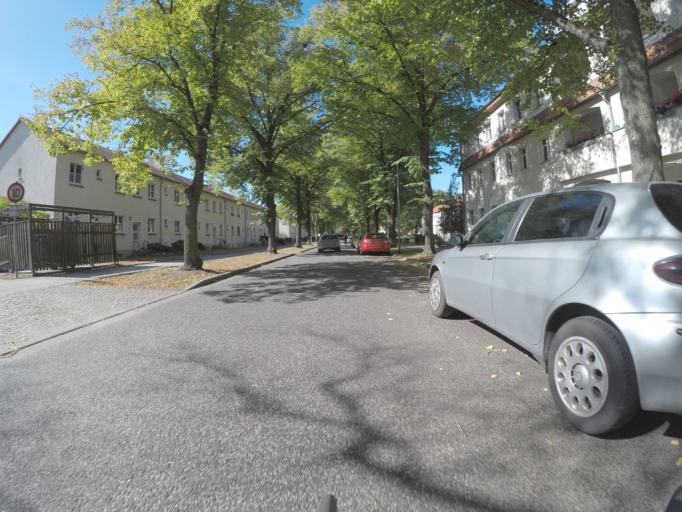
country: DE
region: Brandenburg
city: Hennigsdorf
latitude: 52.6421
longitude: 13.1961
